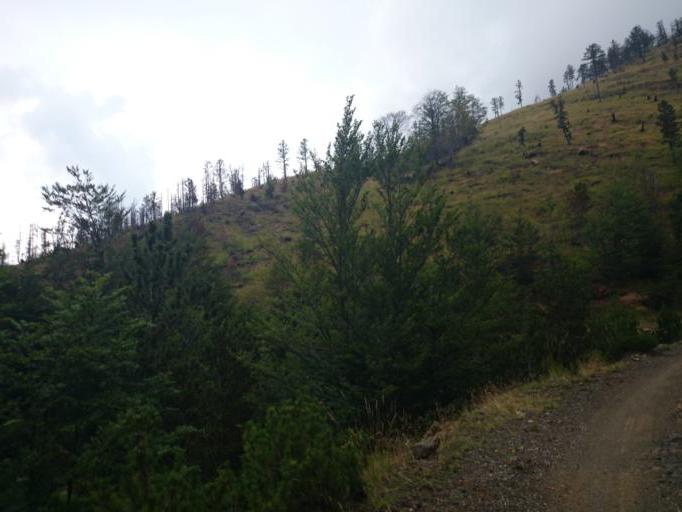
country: AL
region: Lezhe
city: Kurbnesh
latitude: 41.7847
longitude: 20.1554
